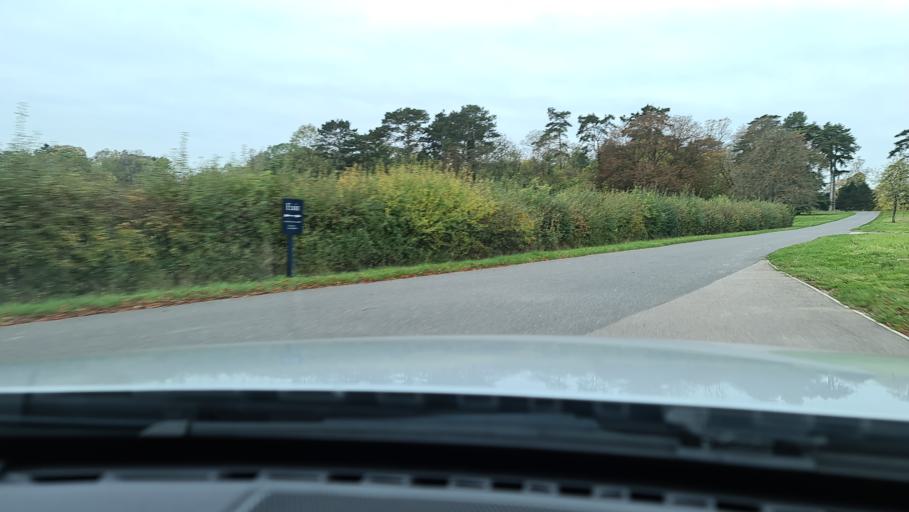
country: GB
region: England
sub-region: Buckinghamshire
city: Waddesdon
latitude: 51.8397
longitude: -0.9201
